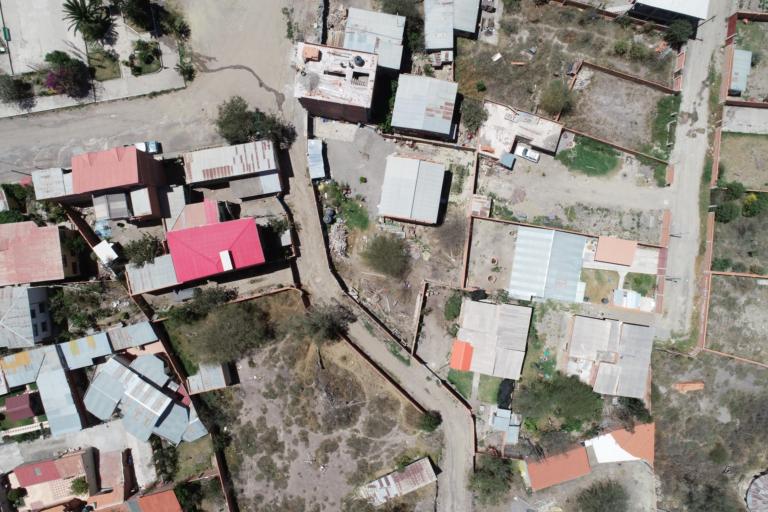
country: BO
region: La Paz
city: La Paz
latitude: -16.6436
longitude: -68.0436
